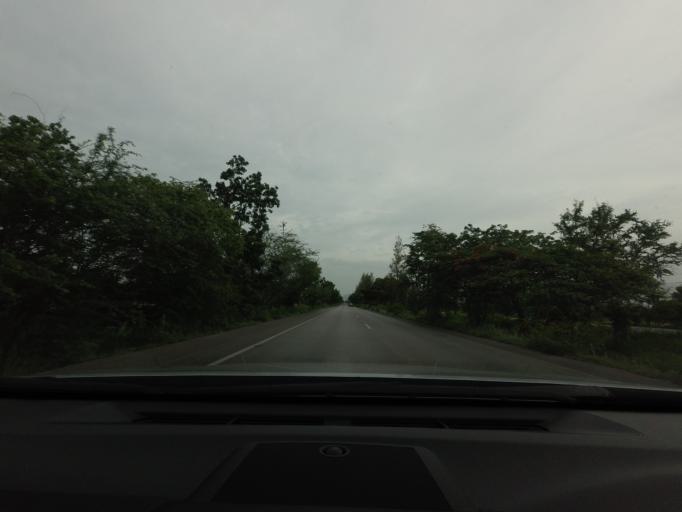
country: TH
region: Phetchaburi
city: Cha-am
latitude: 12.7419
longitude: 99.9297
